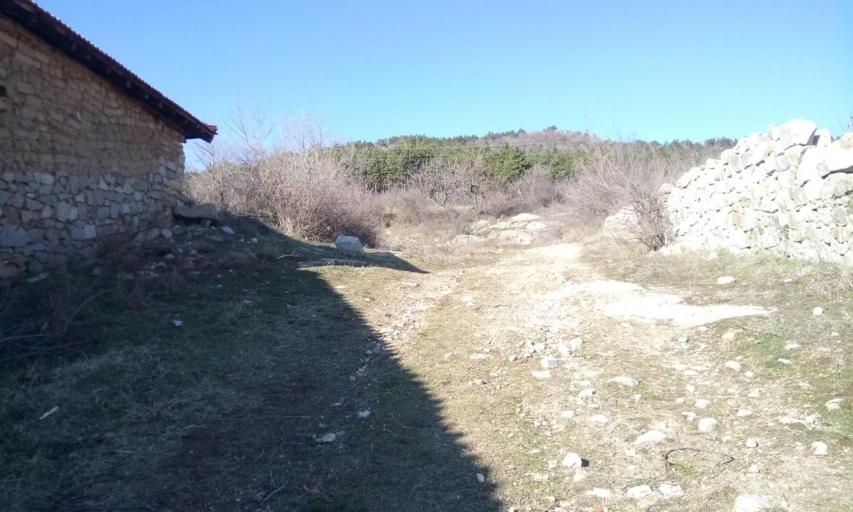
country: BG
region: Plovdiv
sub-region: Obshtina Khisarya
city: Khisarya
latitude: 42.5244
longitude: 24.7191
